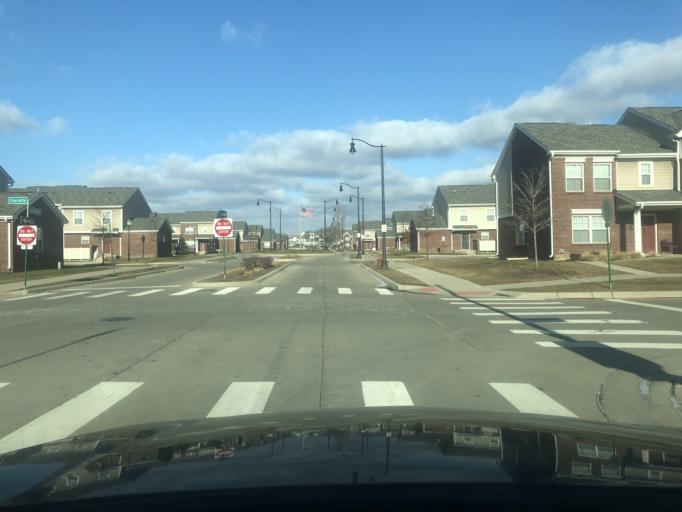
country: US
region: Michigan
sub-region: Wayne County
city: Detroit
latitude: 42.3409
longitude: -83.0654
